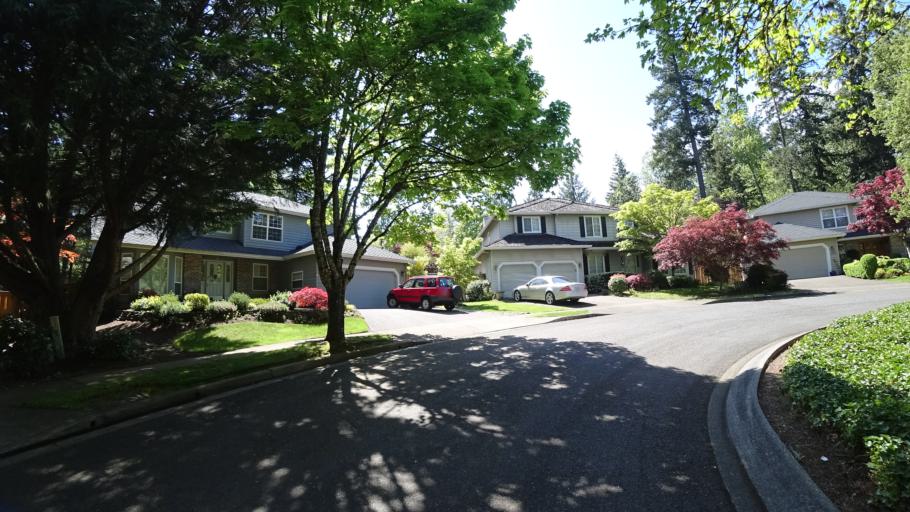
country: US
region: Oregon
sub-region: Washington County
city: Aloha
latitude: 45.4460
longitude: -122.8414
